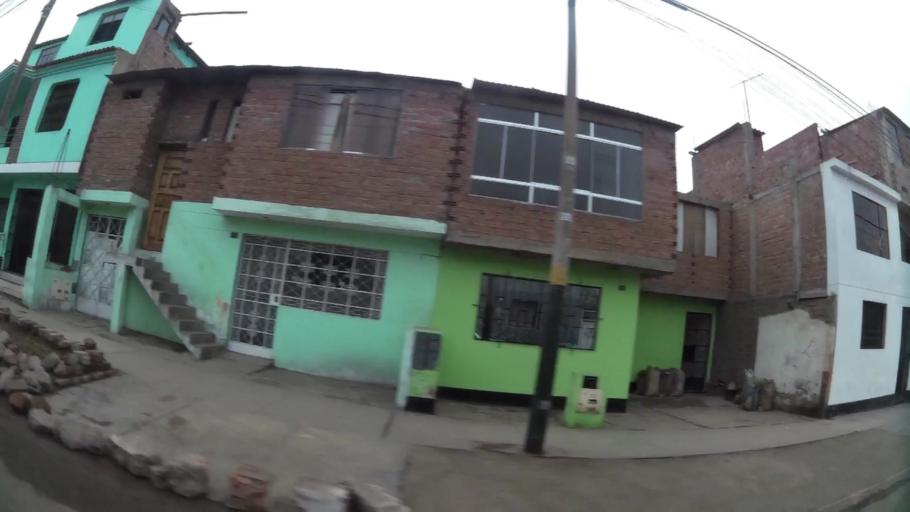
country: PE
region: Lima
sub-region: Lima
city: Surco
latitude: -12.1500
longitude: -76.9788
